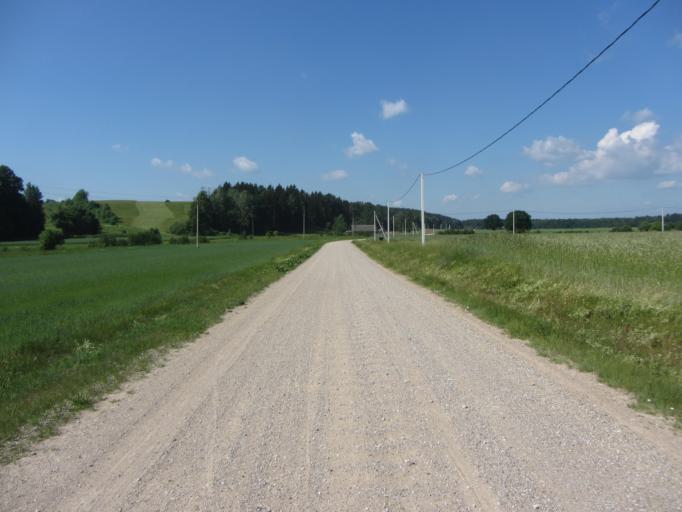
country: LT
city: Prienai
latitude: 54.5483
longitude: 23.9500
